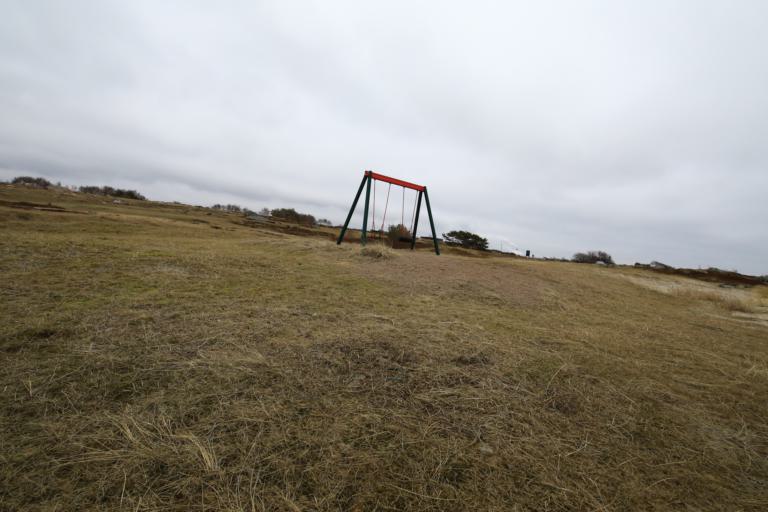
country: SE
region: Halland
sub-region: Kungsbacka Kommun
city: Frillesas
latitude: 57.2443
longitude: 12.1203
